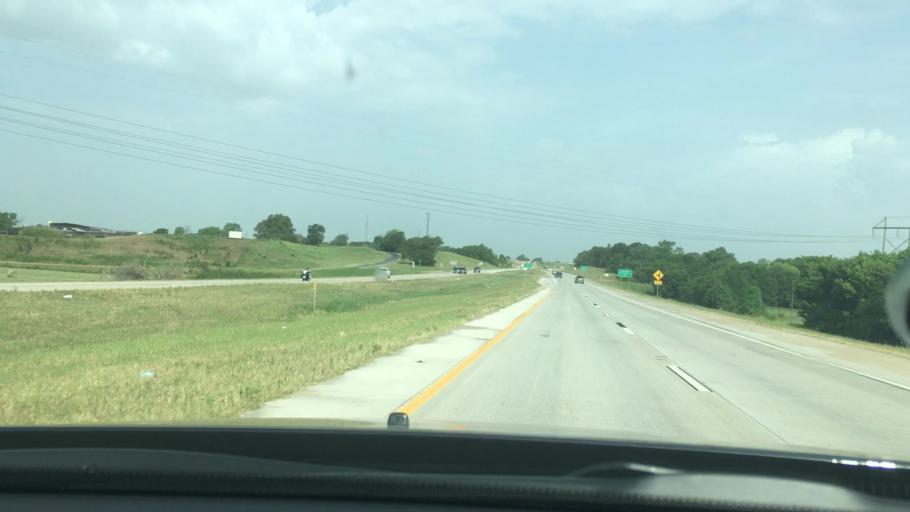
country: US
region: Oklahoma
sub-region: Pontotoc County
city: Ada
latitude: 34.7806
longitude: -96.7131
